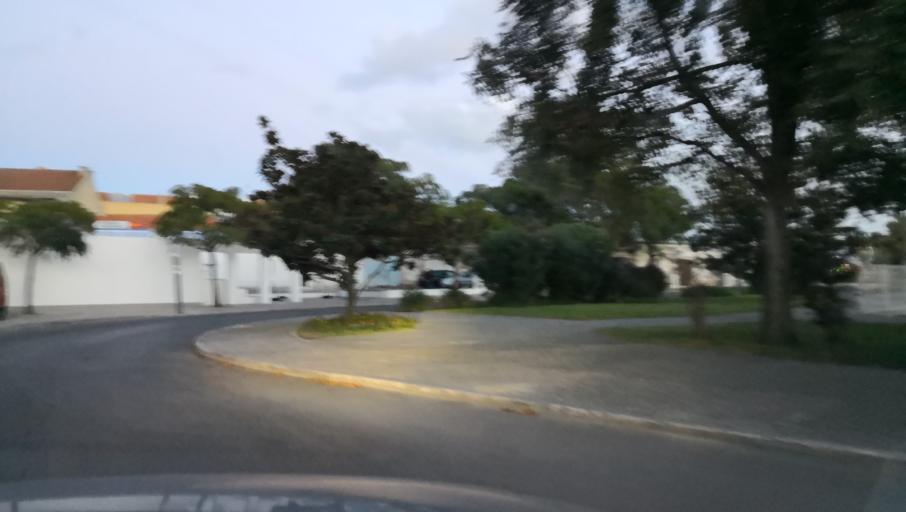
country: PT
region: Setubal
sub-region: Moita
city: Alhos Vedros
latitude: 38.6541
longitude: -9.0288
